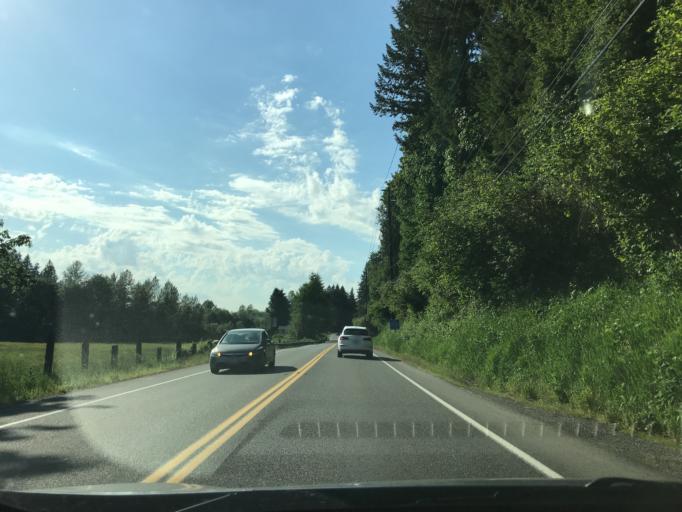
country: US
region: Washington
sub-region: King County
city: Mirrormont
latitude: 47.4587
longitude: -122.0046
